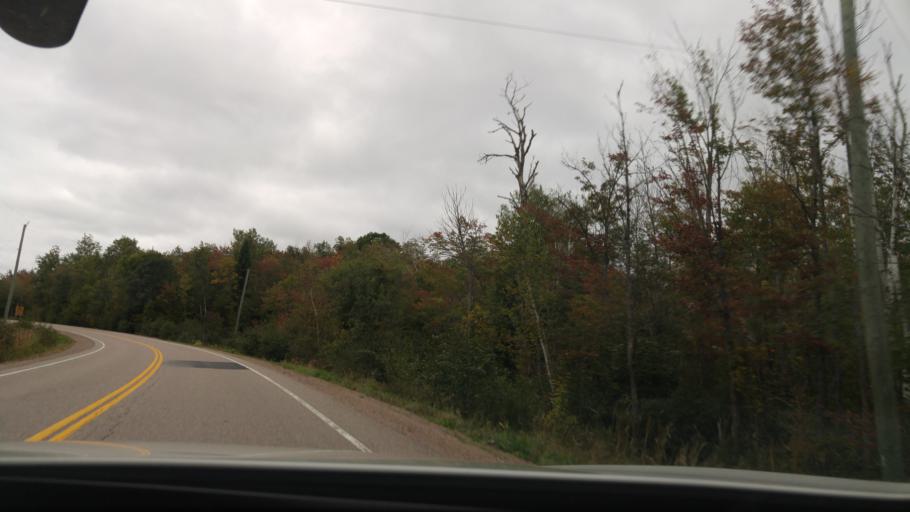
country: CA
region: Ontario
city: Petawawa
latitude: 45.8186
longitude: -77.3222
